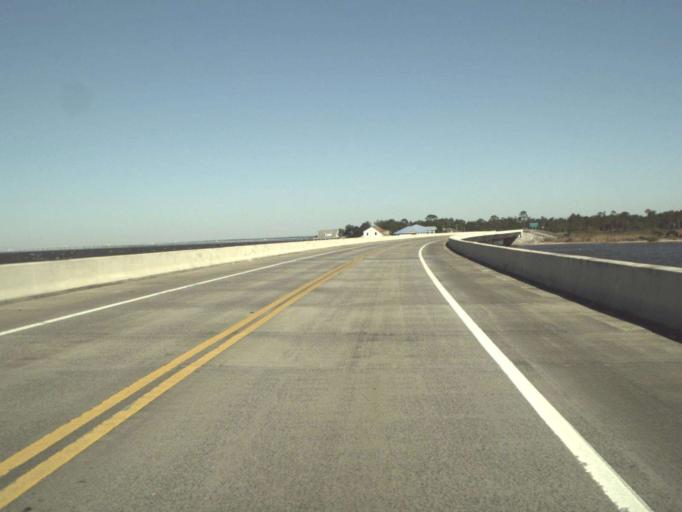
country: US
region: Florida
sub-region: Santa Rosa County
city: Oriole Beach
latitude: 30.4398
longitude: -87.1002
